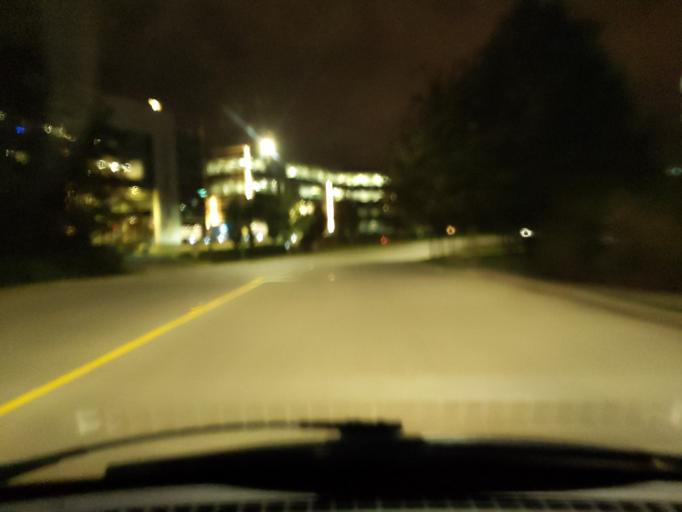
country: CA
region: British Columbia
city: Burnaby
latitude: 49.2597
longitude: -123.0074
